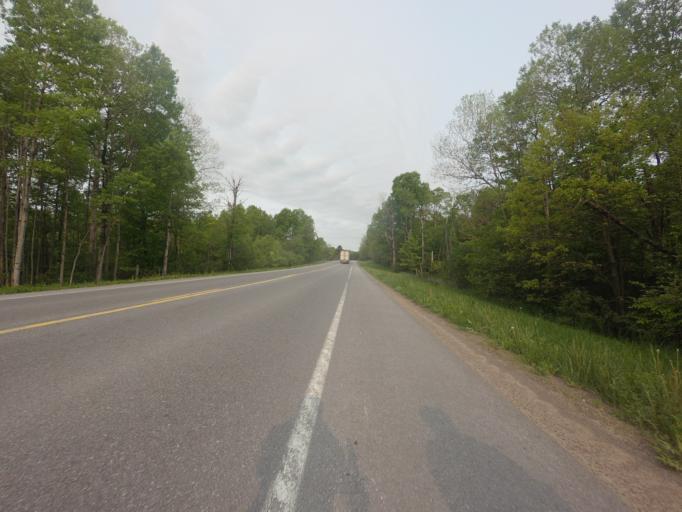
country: US
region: New York
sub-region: Jefferson County
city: Carthage
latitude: 44.0342
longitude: -75.6127
